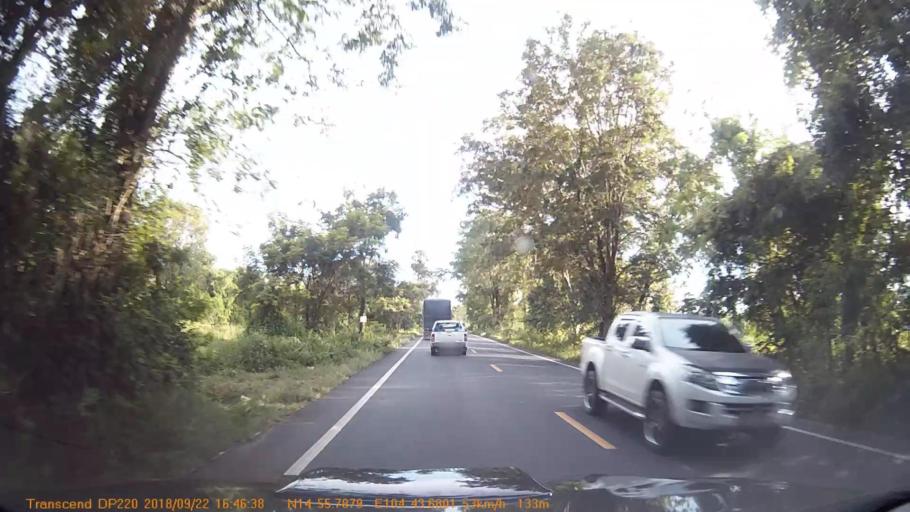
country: TH
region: Sisaket
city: Non Kho
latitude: 14.9297
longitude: 104.7280
